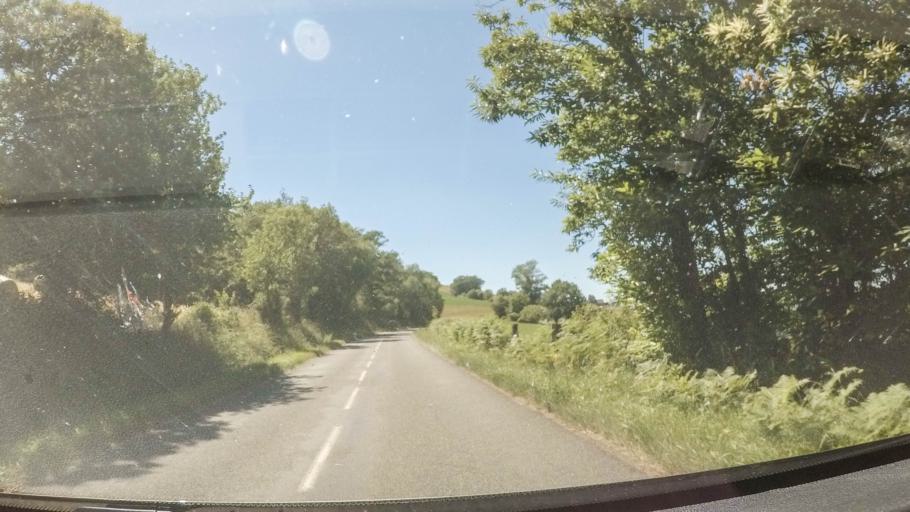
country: FR
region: Midi-Pyrenees
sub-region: Departement de l'Aveyron
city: Saint-Christophe-Vallon
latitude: 44.4692
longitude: 2.3697
